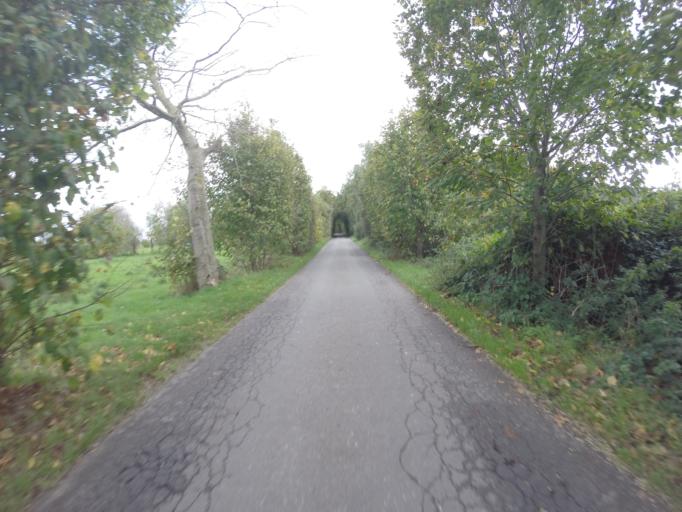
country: BE
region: Flanders
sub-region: Provincie Oost-Vlaanderen
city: Aalter
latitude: 51.0830
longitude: 3.4096
